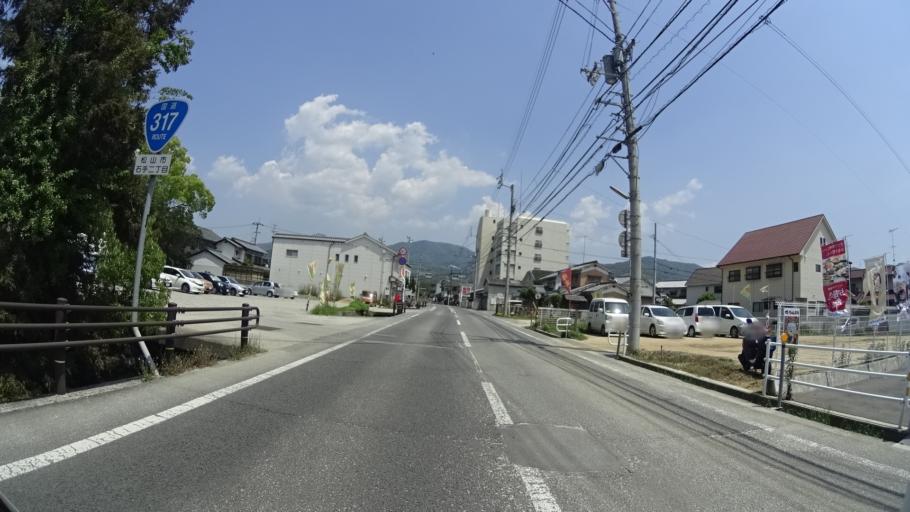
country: JP
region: Ehime
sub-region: Shikoku-chuo Shi
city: Matsuyama
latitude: 33.8468
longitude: 132.7972
